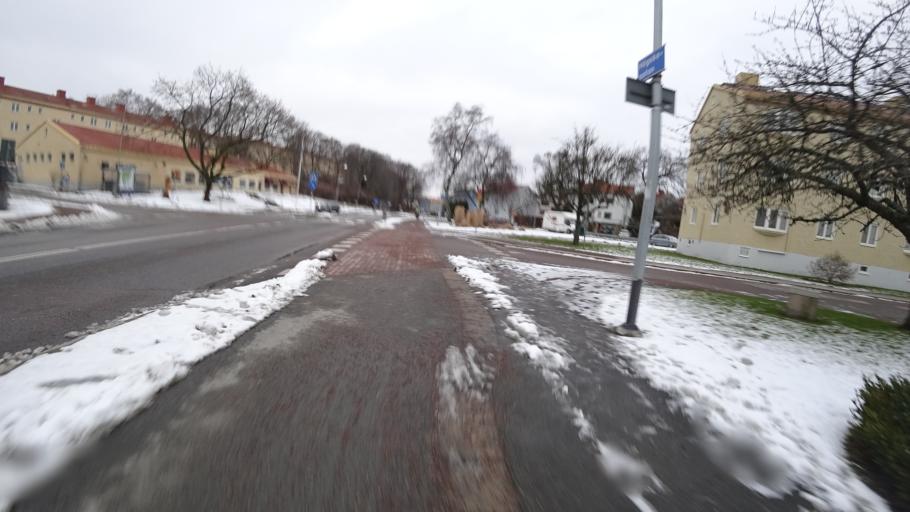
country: SE
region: Vaestra Goetaland
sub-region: Goteborg
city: Majorna
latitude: 57.6769
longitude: 11.9287
